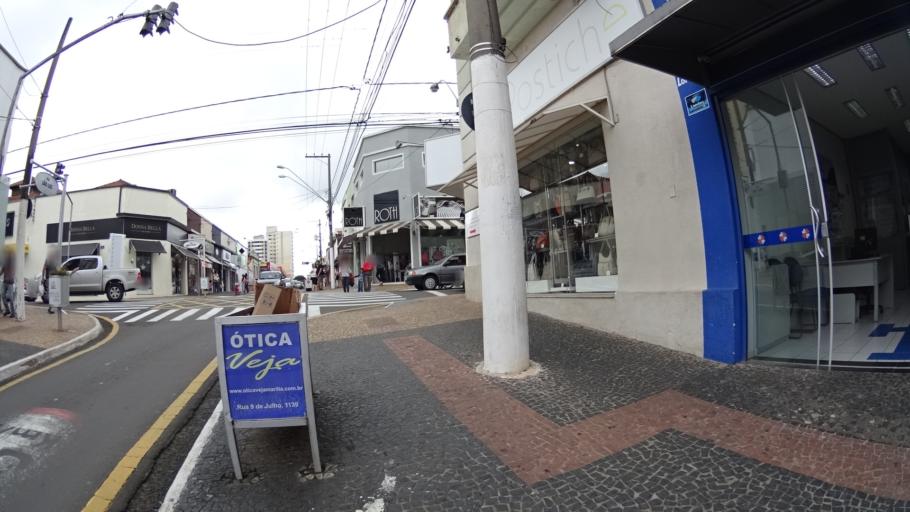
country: BR
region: Sao Paulo
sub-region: Marilia
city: Marilia
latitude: -22.2187
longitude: -49.9499
